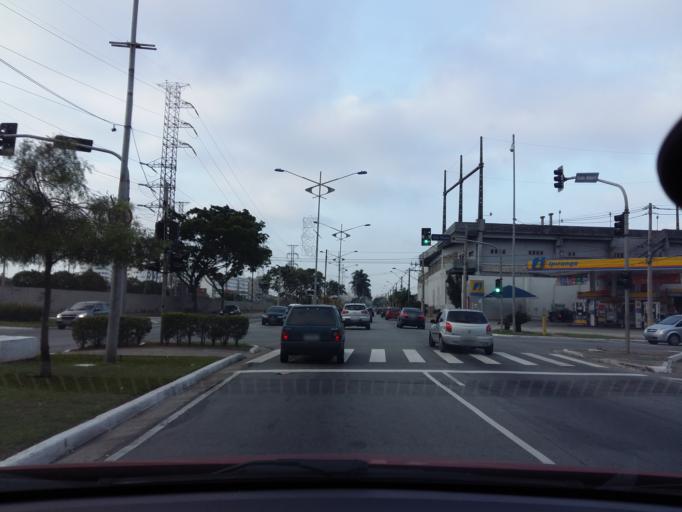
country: BR
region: Sao Paulo
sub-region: Sao Caetano Do Sul
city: Sao Caetano do Sul
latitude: -23.6222
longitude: -46.5818
